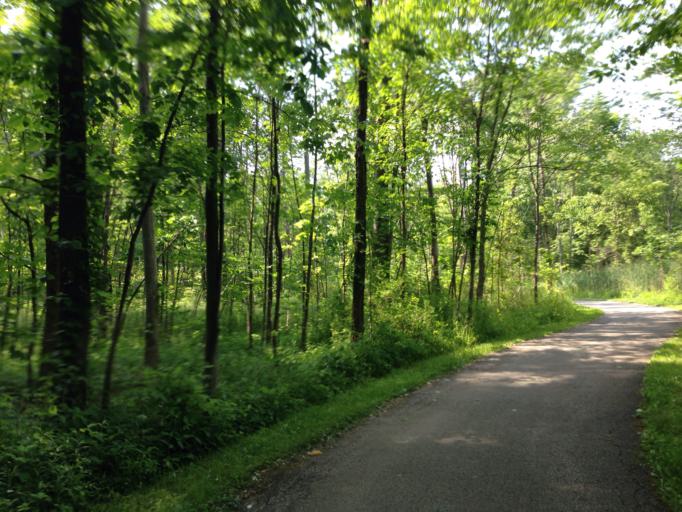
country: US
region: Ohio
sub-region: Cuyahoga County
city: Olmsted Falls
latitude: 41.4036
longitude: -81.8840
